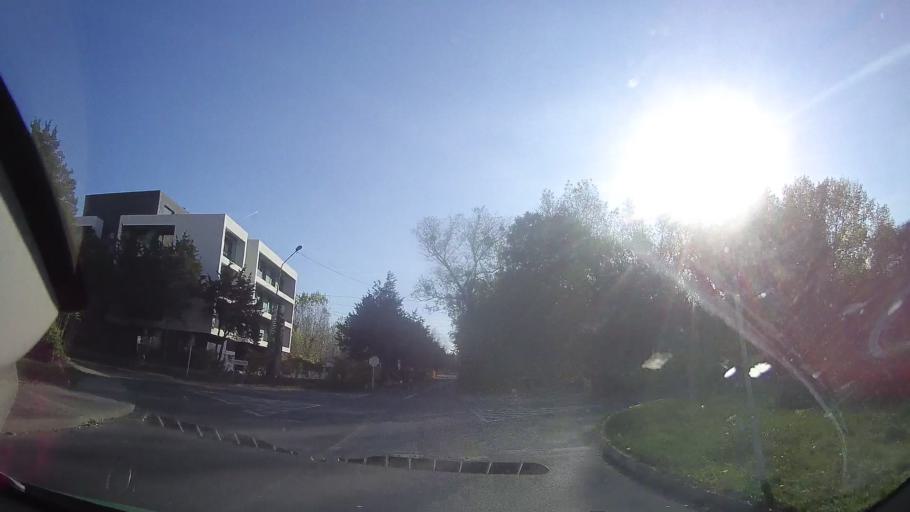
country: RO
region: Constanta
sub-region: Comuna Douazeci si Trei August
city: Douazeci si Trei August
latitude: 43.8599
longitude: 28.5982
